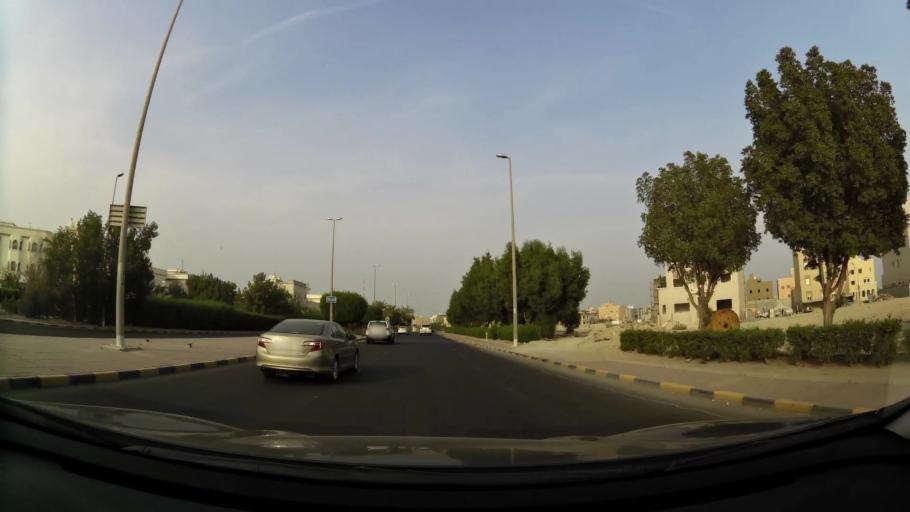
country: KW
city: Al Funaytis
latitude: 29.2269
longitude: 48.0823
